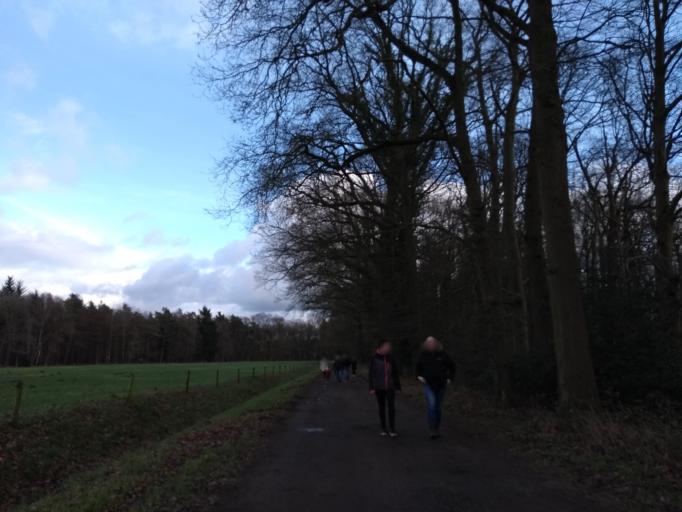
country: NL
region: Overijssel
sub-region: Gemeente Enschede
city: Enschede
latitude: 52.2578
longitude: 6.8708
